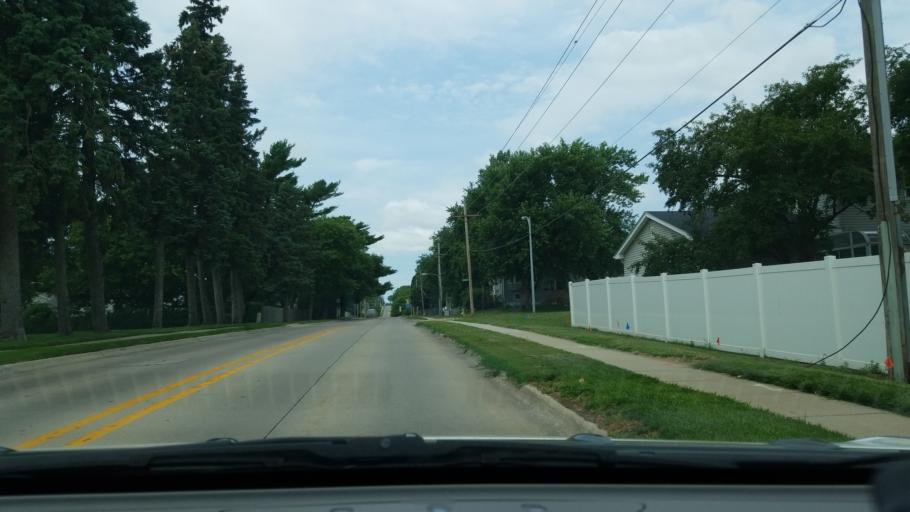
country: US
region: Nebraska
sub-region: Sarpy County
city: Papillion
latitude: 41.1436
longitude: -96.0296
